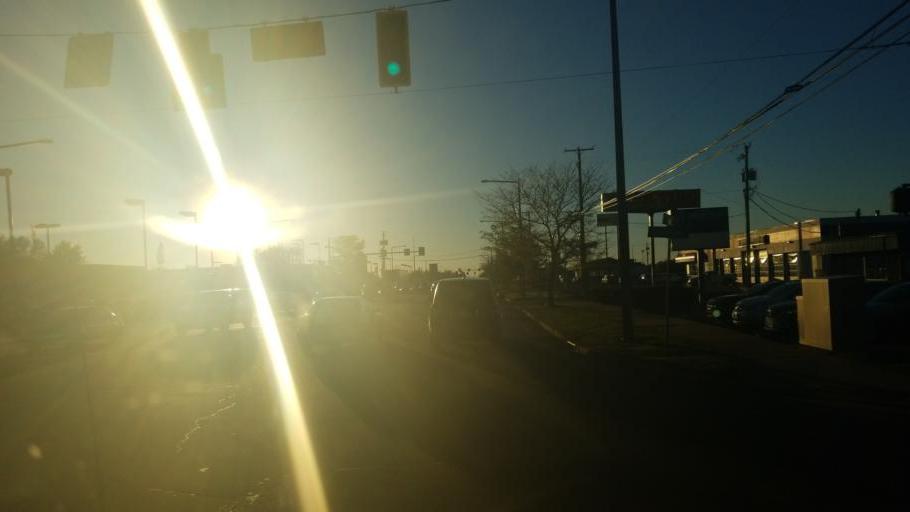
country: US
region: Ohio
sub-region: Stark County
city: Alliance
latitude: 40.9020
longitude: -81.1348
